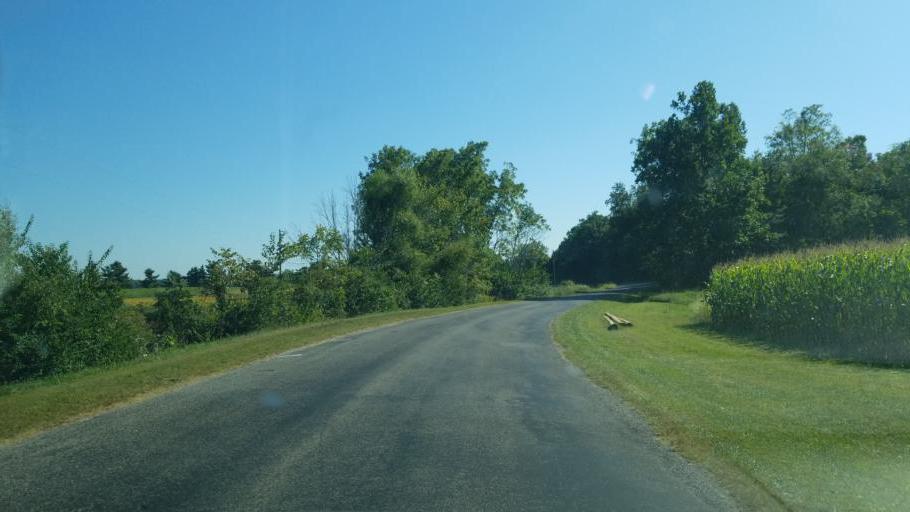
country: US
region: Ohio
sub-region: Champaign County
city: North Lewisburg
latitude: 40.1865
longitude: -83.6169
